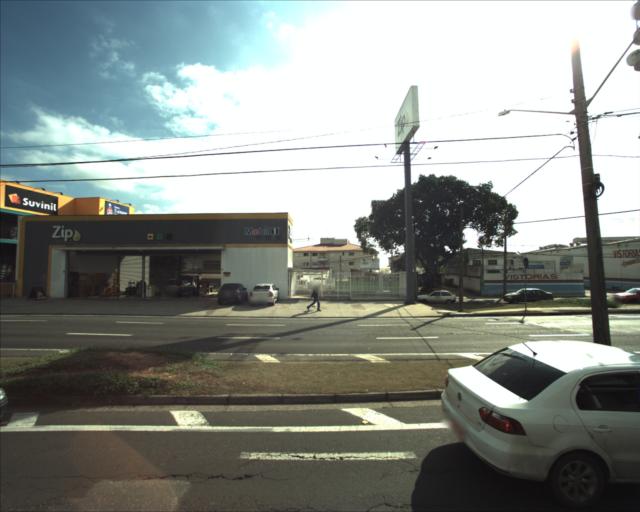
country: BR
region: Sao Paulo
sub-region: Sorocaba
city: Sorocaba
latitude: -23.5131
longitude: -47.4890
